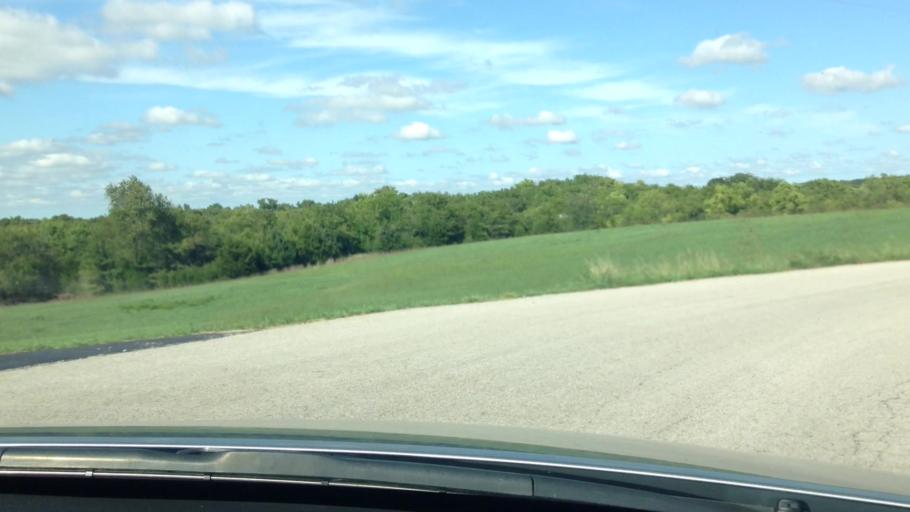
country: US
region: Missouri
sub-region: Clay County
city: Smithville
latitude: 39.3400
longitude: -94.6674
